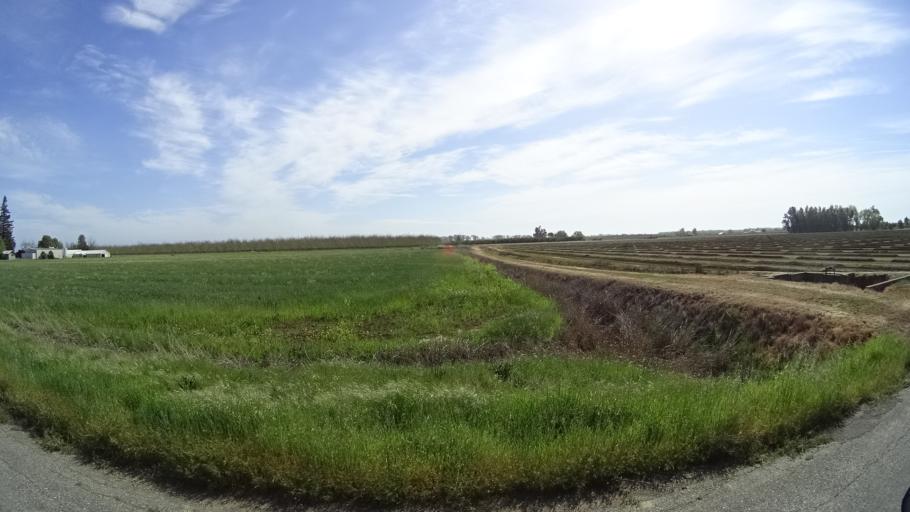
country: US
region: California
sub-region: Glenn County
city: Hamilton City
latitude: 39.6561
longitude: -122.0181
